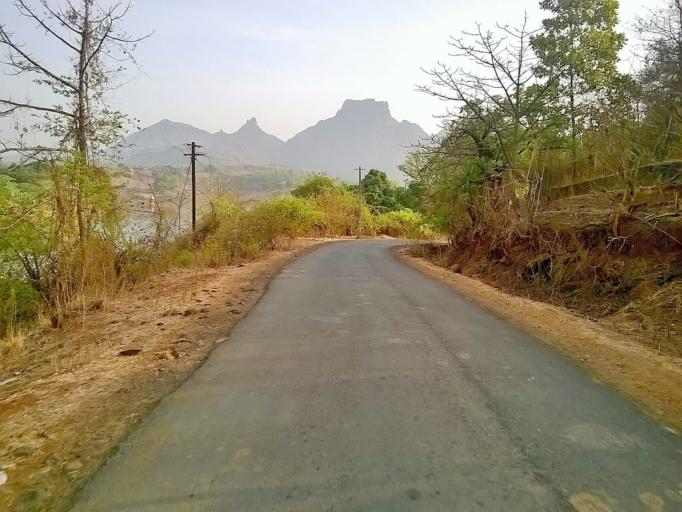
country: IN
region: Maharashtra
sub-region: Raigarh
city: Matheran
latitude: 19.0276
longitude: 73.2439
